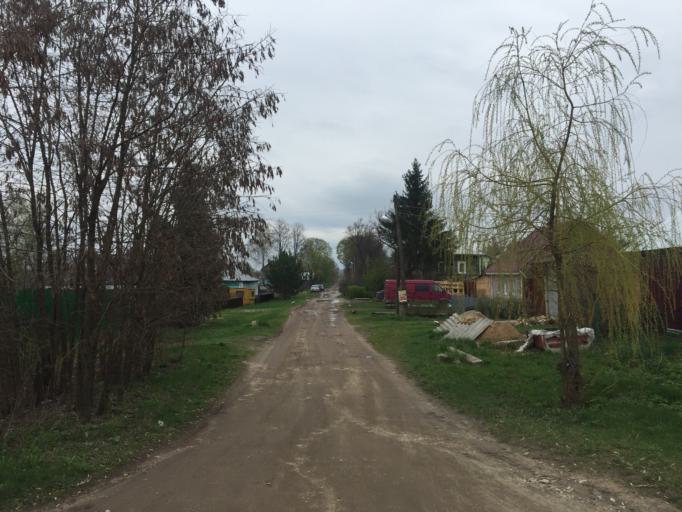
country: RU
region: Tula
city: Krapivna
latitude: 53.9438
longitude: 37.1516
